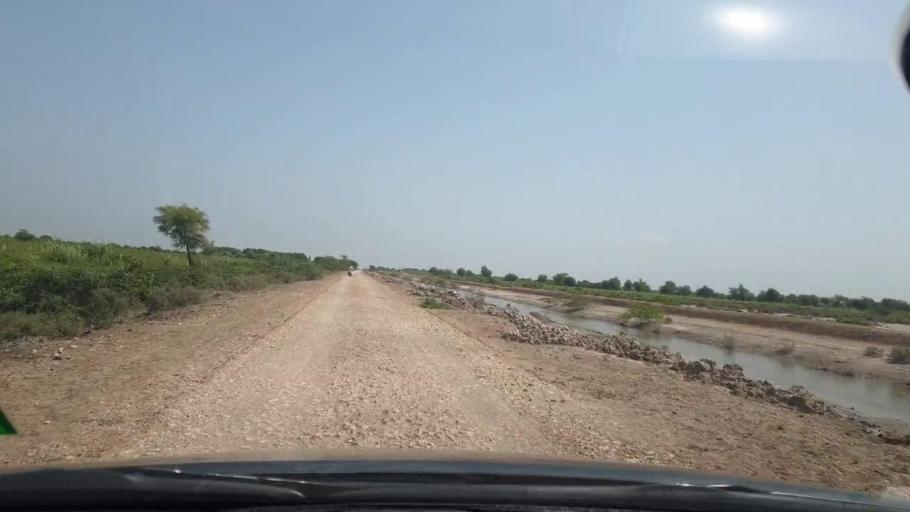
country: PK
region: Sindh
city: Tando Bago
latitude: 24.8942
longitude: 69.0925
